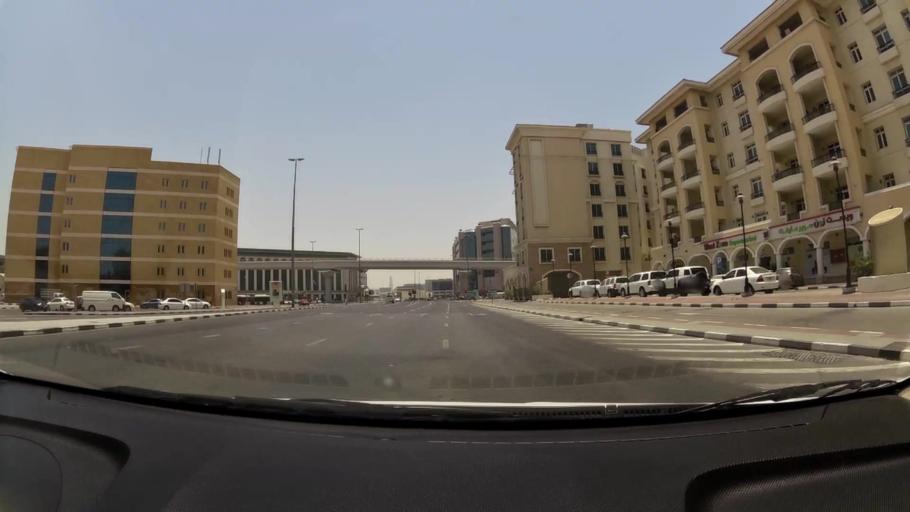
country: AE
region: Ash Shariqah
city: Sharjah
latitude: 25.2716
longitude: 55.3300
